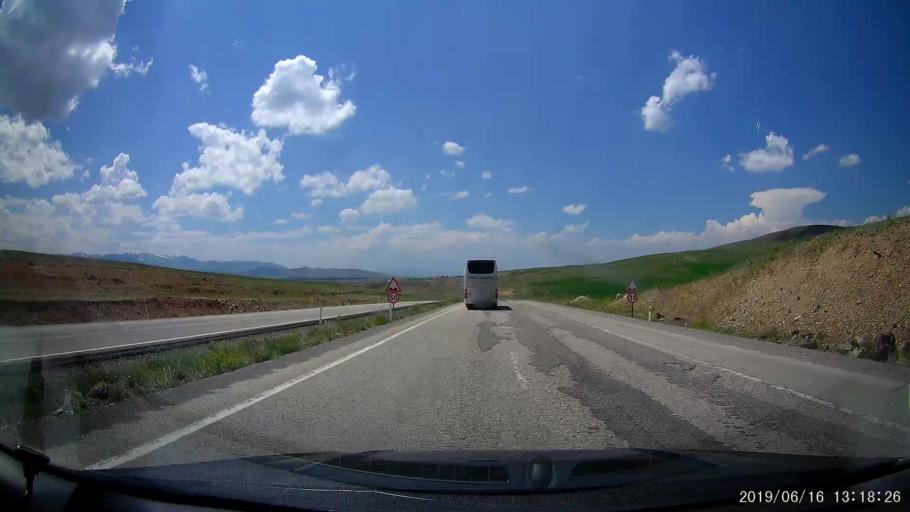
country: TR
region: Agri
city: Taslicay
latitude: 39.6306
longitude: 43.4307
